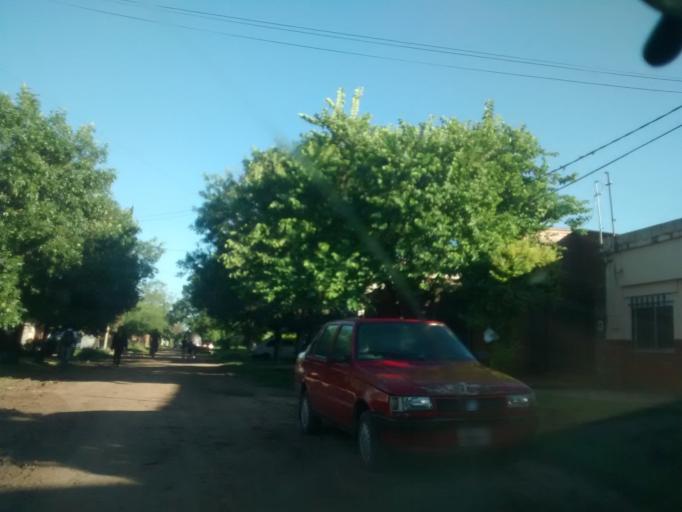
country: AR
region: Chaco
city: Resistencia
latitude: -27.4625
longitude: -59.0012
